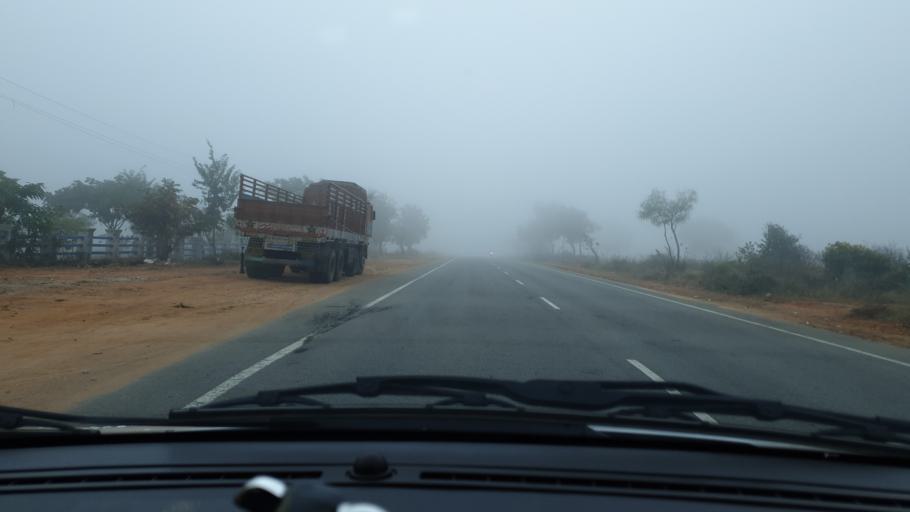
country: IN
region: Telangana
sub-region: Mahbubnagar
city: Nagar Karnul
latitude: 16.6891
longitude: 78.5215
